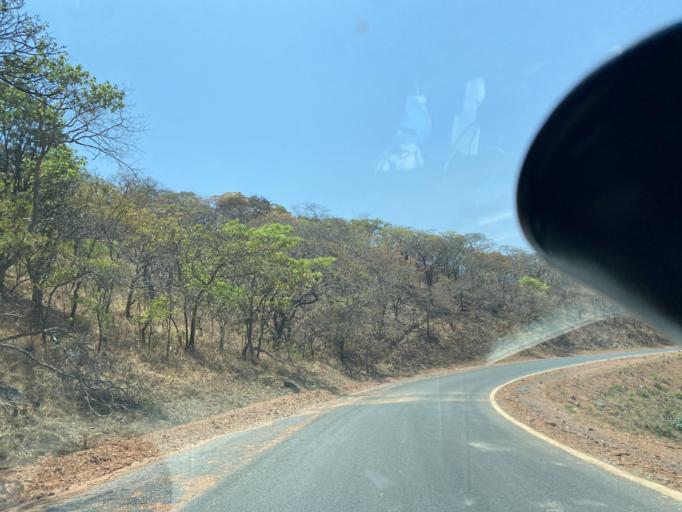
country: ZM
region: Lusaka
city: Kafue
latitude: -15.8584
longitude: 28.4214
